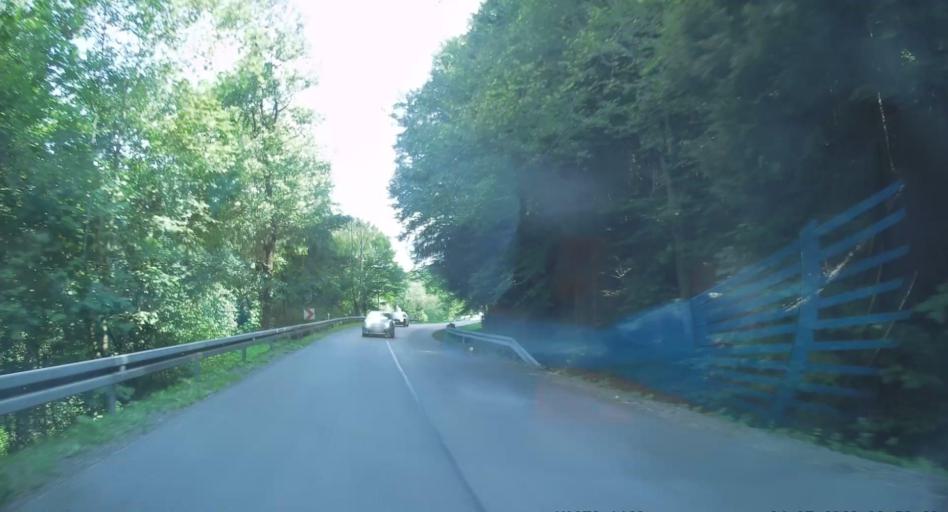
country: PL
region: Lesser Poland Voivodeship
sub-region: Powiat tarnowski
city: Zakliczyn
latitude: 49.7798
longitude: 20.7827
